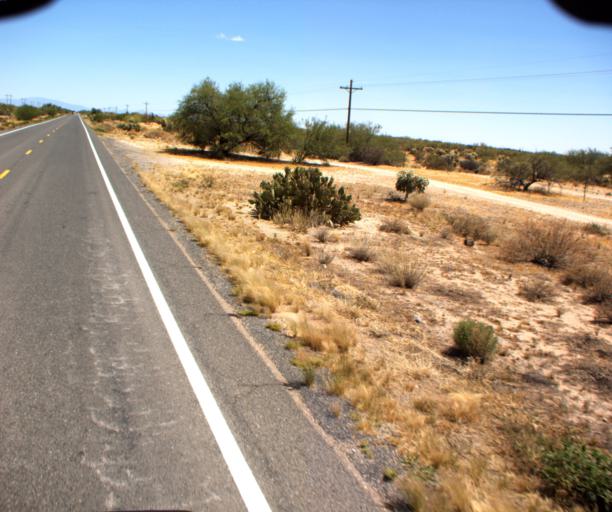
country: US
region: Arizona
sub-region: Pinal County
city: Florence
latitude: 32.9221
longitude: -111.2991
